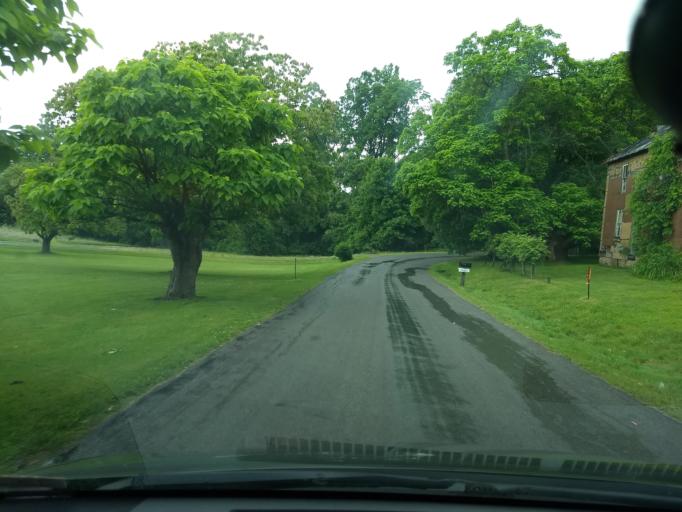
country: US
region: Pennsylvania
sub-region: Armstrong County
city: Orchard Hills
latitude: 40.5531
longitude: -79.5032
